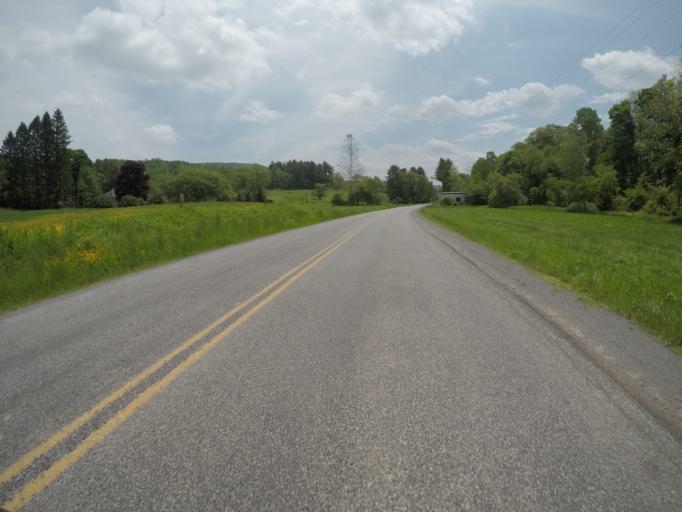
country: US
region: New York
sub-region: Delaware County
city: Stamford
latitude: 42.2056
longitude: -74.6781
